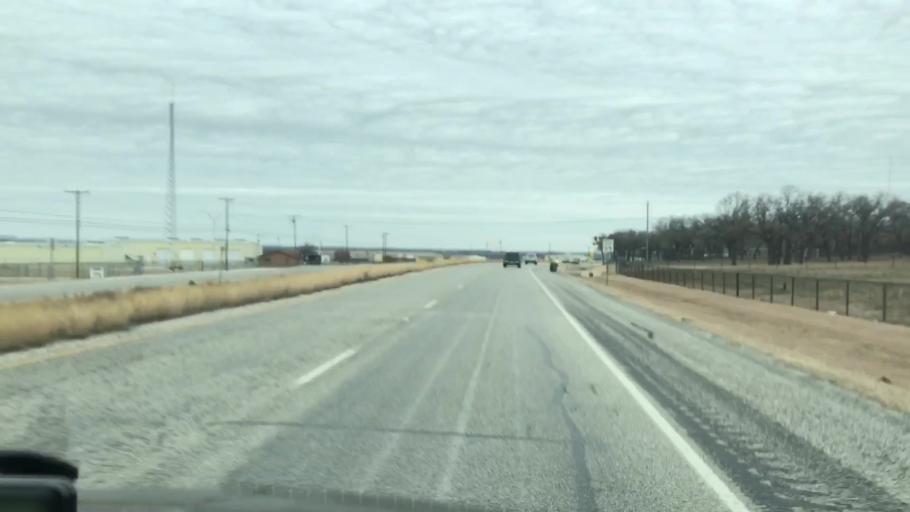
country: US
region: Texas
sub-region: Jack County
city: Jacksboro
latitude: 33.1944
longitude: -98.1431
